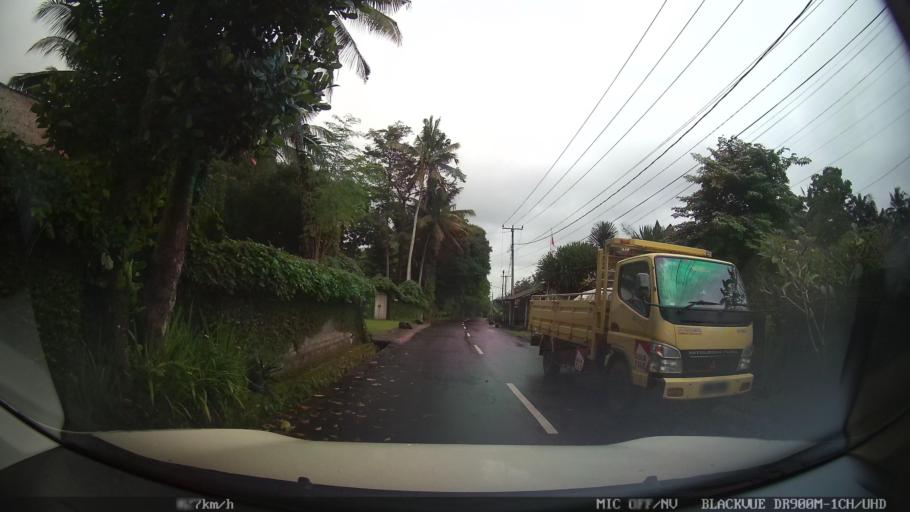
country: ID
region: Bali
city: Pegongan
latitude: -8.4909
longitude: 115.2397
